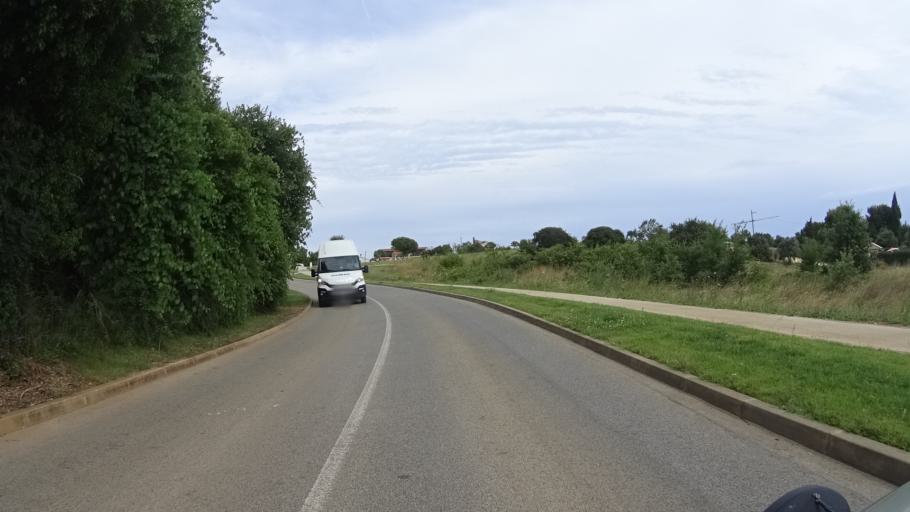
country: HR
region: Istarska
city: Medulin
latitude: 44.8254
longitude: 13.8898
